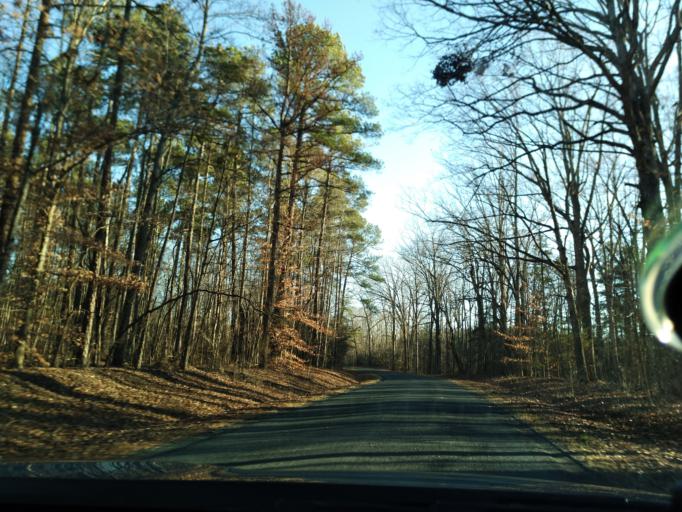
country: US
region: Virginia
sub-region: Appomattox County
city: Appomattox
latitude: 37.3911
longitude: -78.6577
